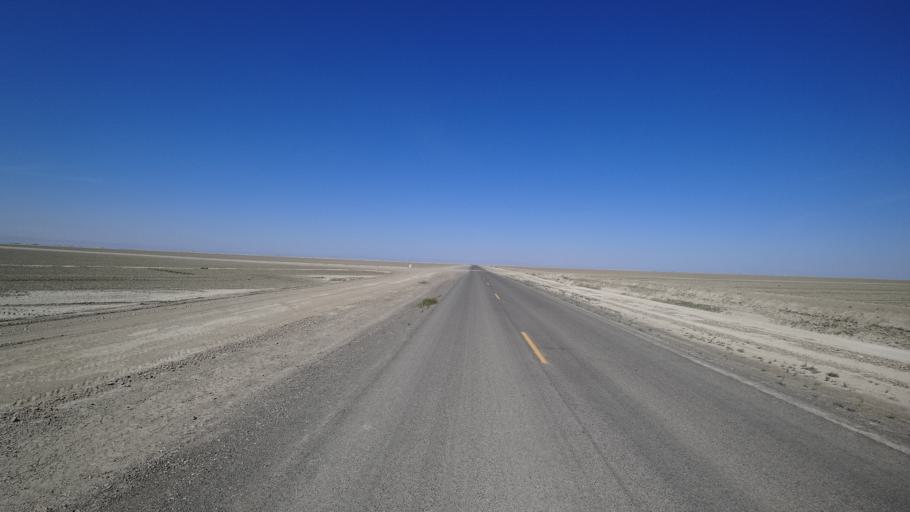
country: US
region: California
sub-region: Tulare County
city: Alpaugh
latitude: 35.8913
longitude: -119.5546
